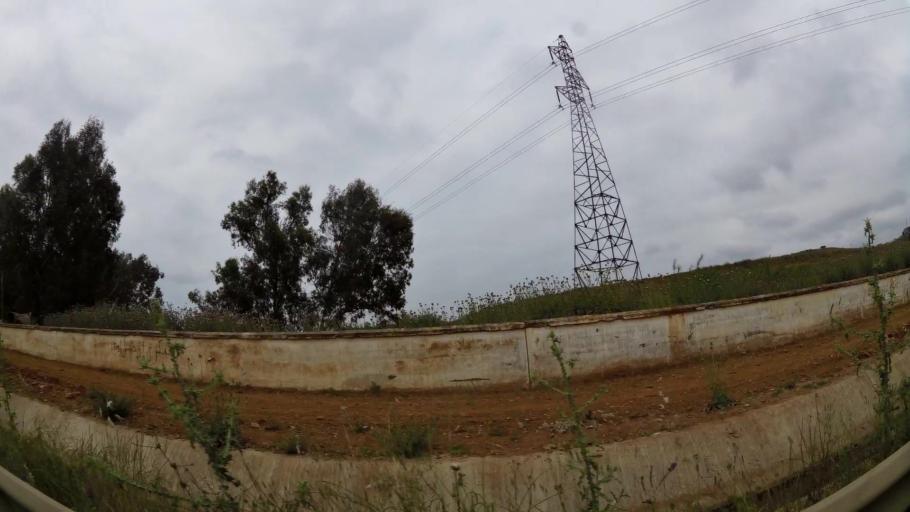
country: MA
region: Rabat-Sale-Zemmour-Zaer
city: Sale
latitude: 34.0111
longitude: -6.7854
